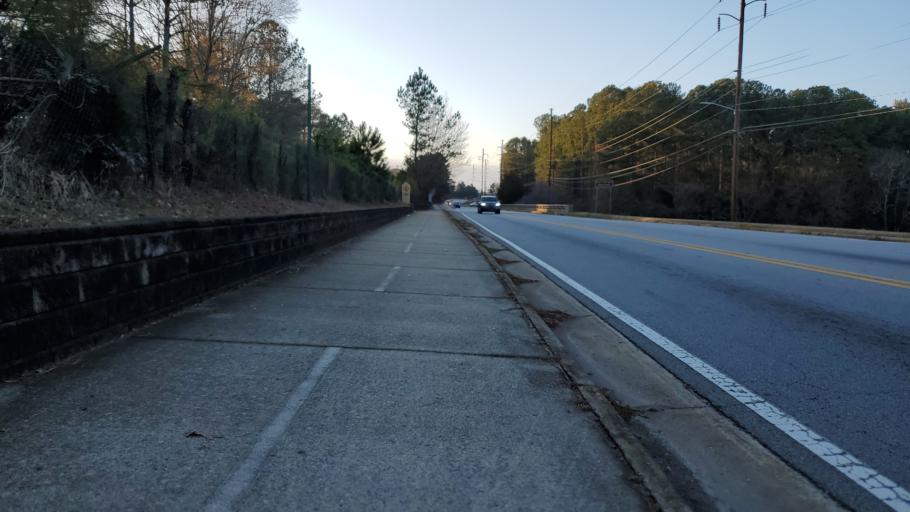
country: US
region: Georgia
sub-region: DeKalb County
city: Stone Mountain
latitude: 33.8138
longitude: -84.1764
